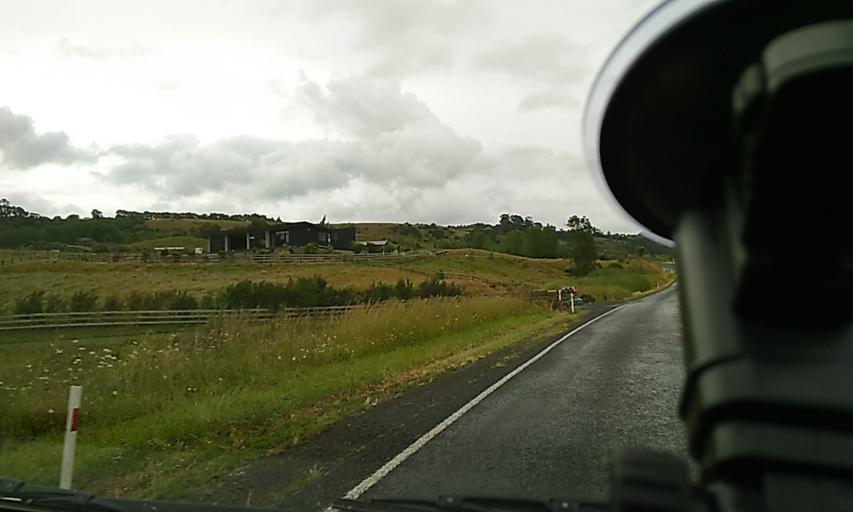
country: NZ
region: Auckland
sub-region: Auckland
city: Pukekohe East
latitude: -37.3151
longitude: 174.9535
